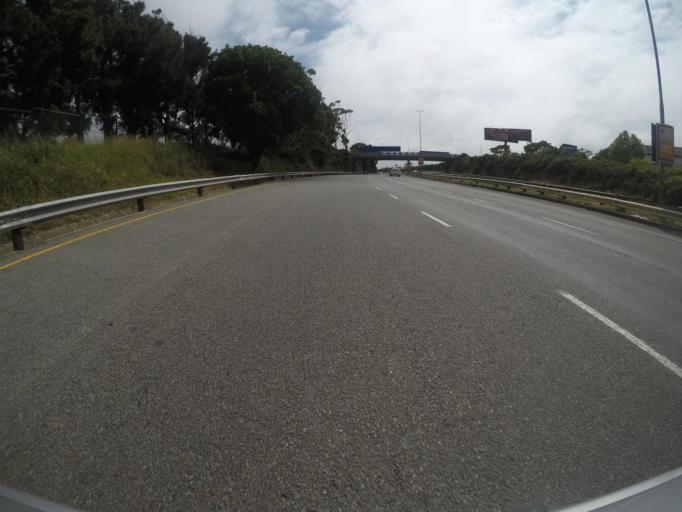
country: ZA
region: Eastern Cape
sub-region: Buffalo City Metropolitan Municipality
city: East London
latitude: -32.9991
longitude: 27.9145
